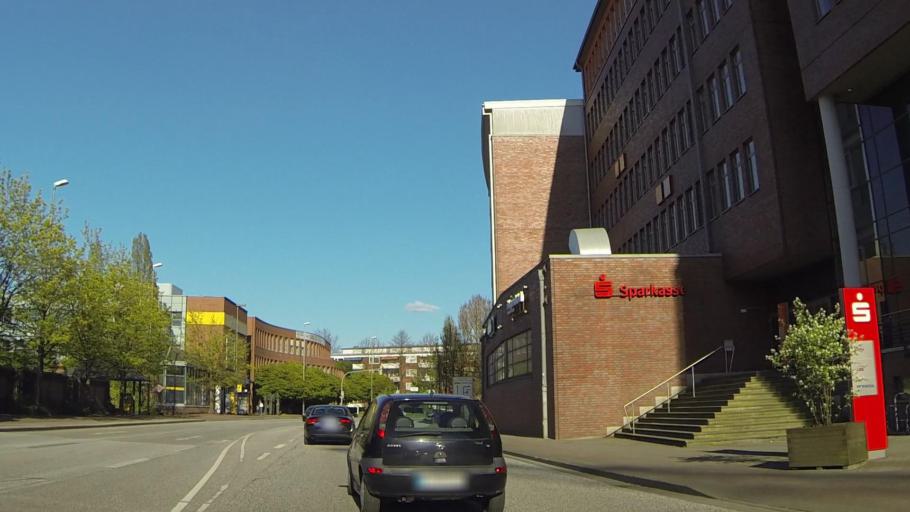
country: DE
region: Schleswig-Holstein
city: Pinneberg
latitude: 53.6626
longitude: 9.7974
